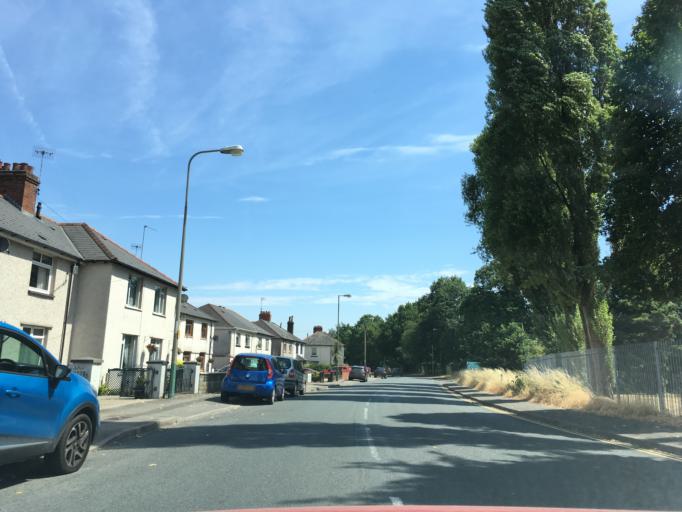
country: GB
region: Wales
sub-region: Caerphilly County Borough
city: Risca
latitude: 51.6019
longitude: -3.0873
